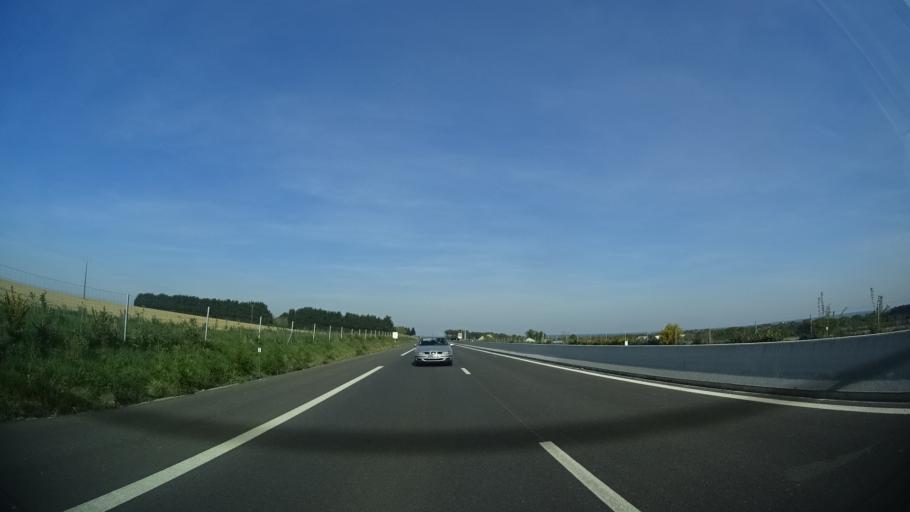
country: FR
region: Brittany
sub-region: Departement du Morbihan
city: Saint-Jean-la-Poterie
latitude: 47.6132
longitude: -2.1386
